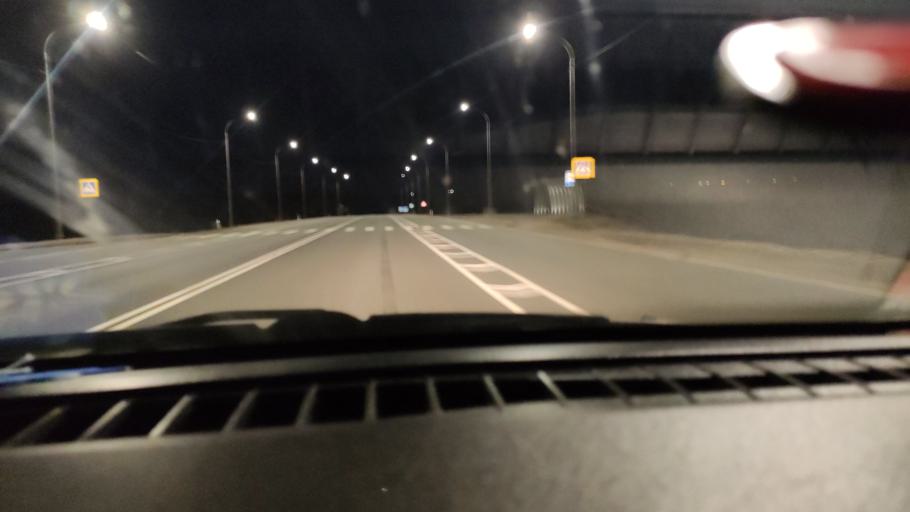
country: RU
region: Saratov
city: Shikhany
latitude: 52.1288
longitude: 47.2342
